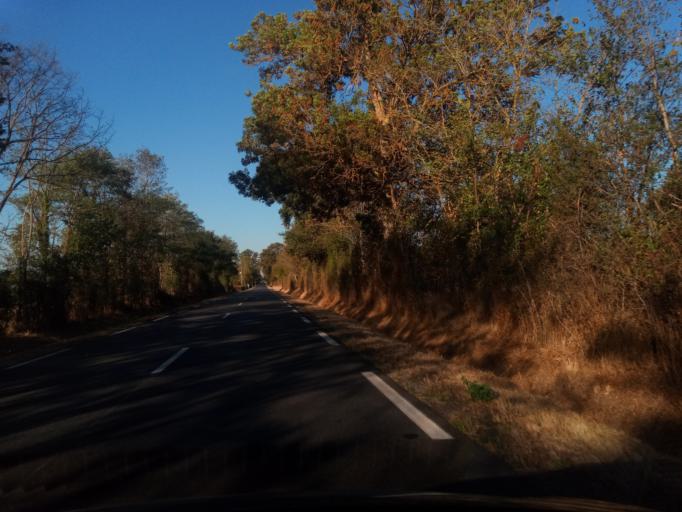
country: FR
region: Poitou-Charentes
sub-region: Departement de la Vienne
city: Montmorillon
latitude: 46.4129
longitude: 0.8232
